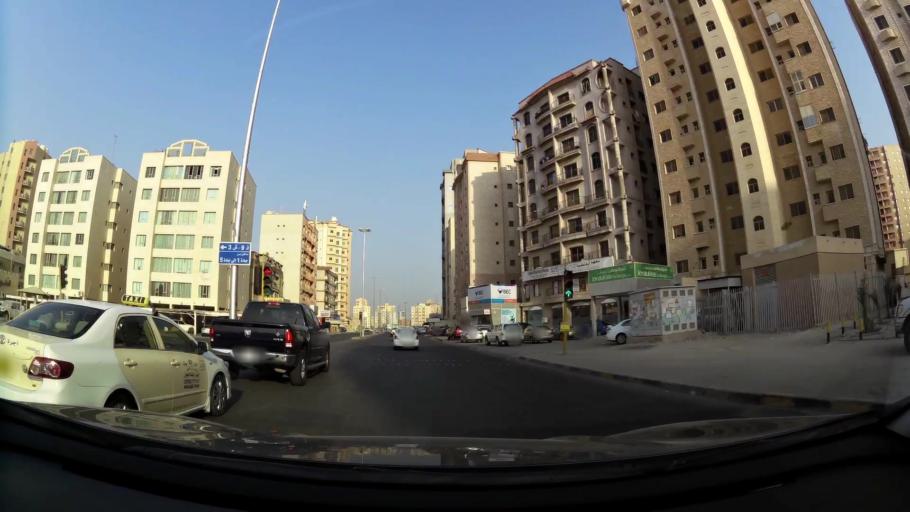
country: KW
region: Muhafazat Hawalli
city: As Salimiyah
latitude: 29.3319
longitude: 48.0605
